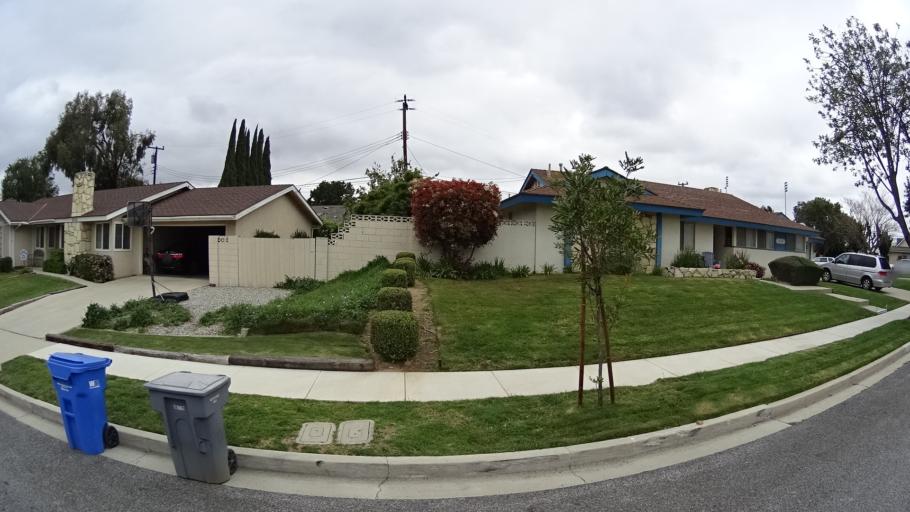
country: US
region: California
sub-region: Ventura County
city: Thousand Oaks
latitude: 34.2093
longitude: -118.8732
